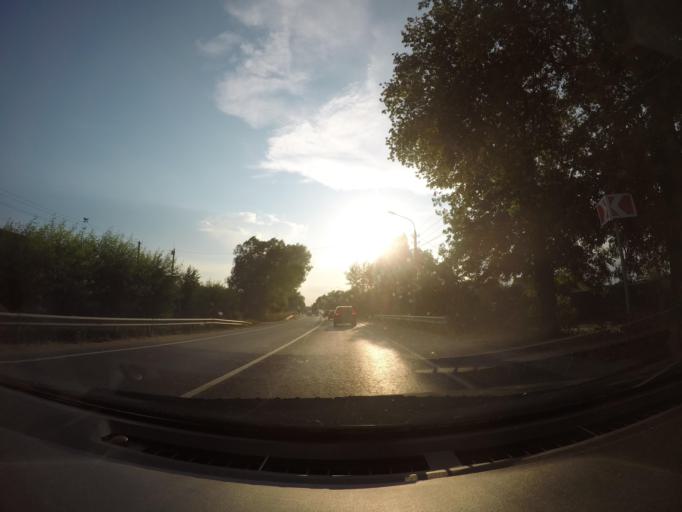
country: RU
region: Moskovskaya
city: Gzhel'
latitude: 55.6068
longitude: 38.4136
